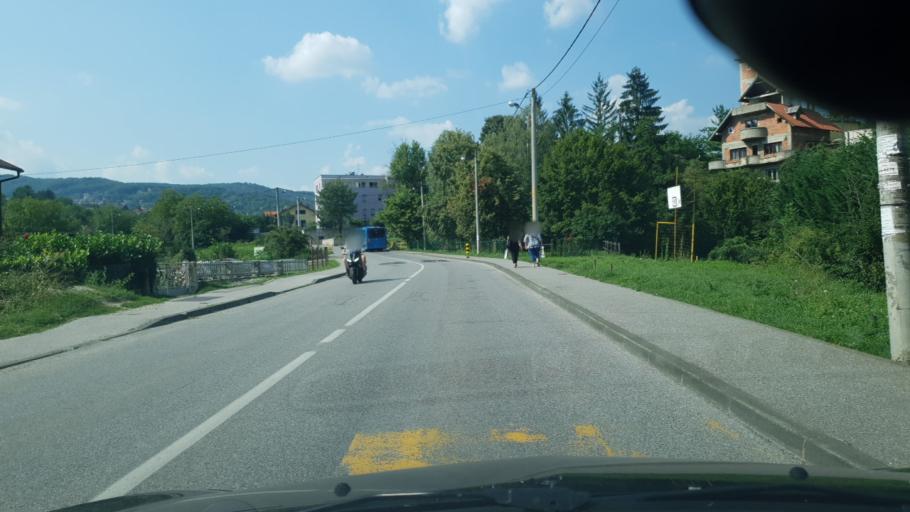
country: HR
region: Grad Zagreb
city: Stenjevec
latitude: 45.8233
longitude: 15.9066
